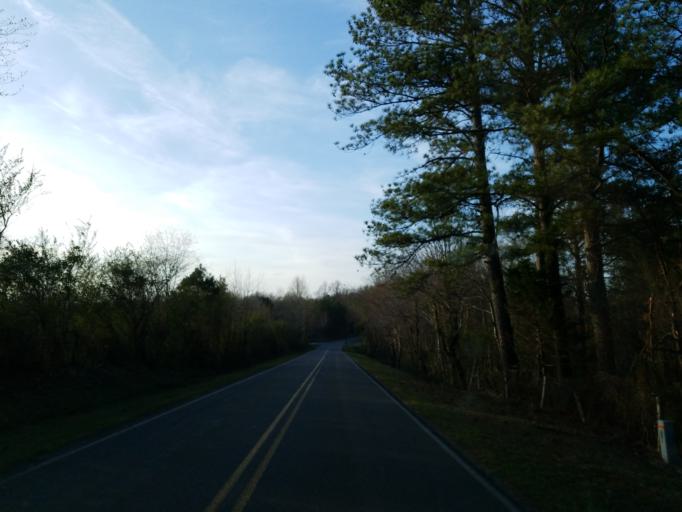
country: US
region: Georgia
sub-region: Pickens County
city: Jasper
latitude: 34.4866
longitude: -84.5127
